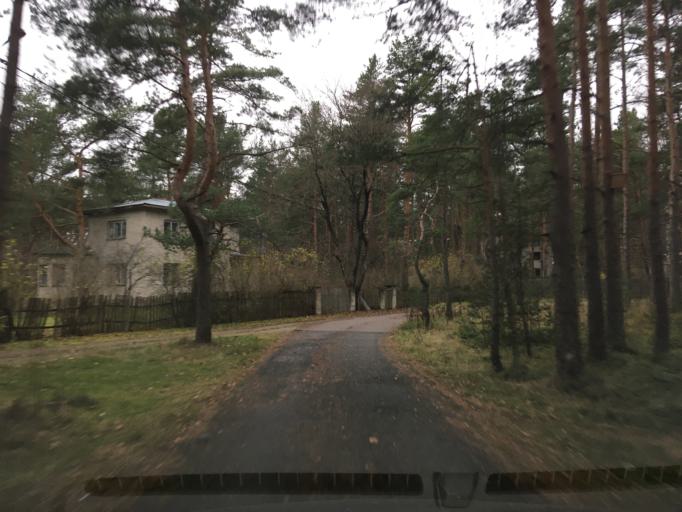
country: EE
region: Harju
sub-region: Tallinna linn
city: Tallinn
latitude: 59.3756
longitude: 24.6995
